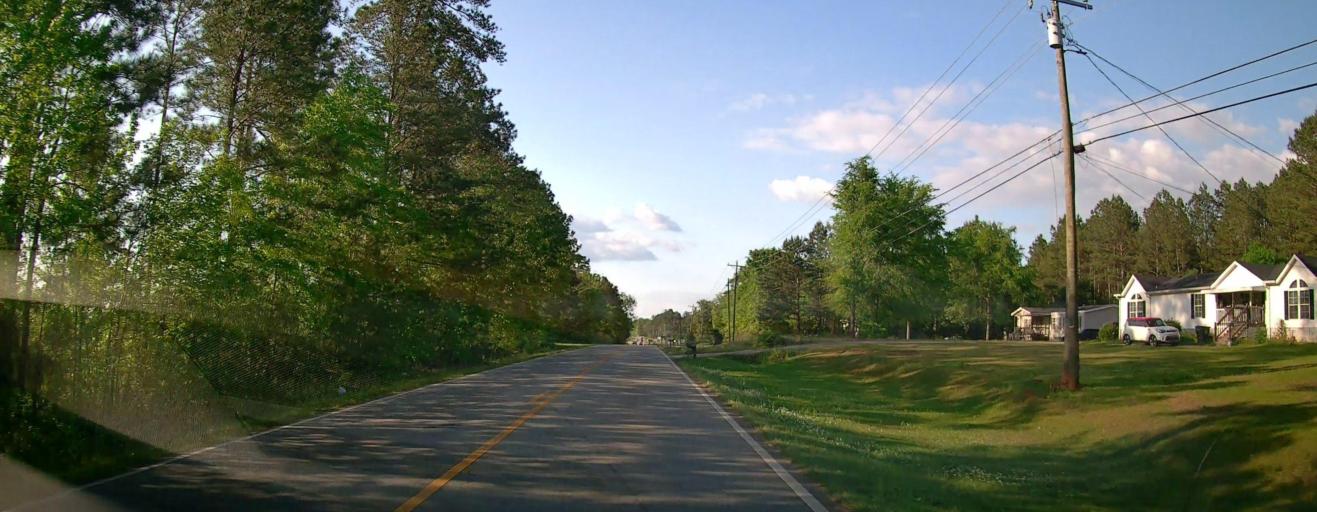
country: US
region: Georgia
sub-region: Putnam County
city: Eatonton
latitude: 33.2661
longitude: -83.3013
